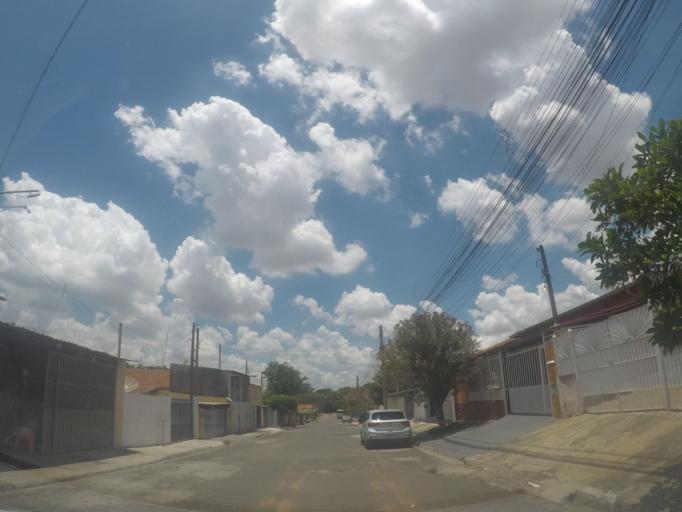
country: BR
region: Sao Paulo
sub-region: Sumare
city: Sumare
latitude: -22.8146
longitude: -47.2353
